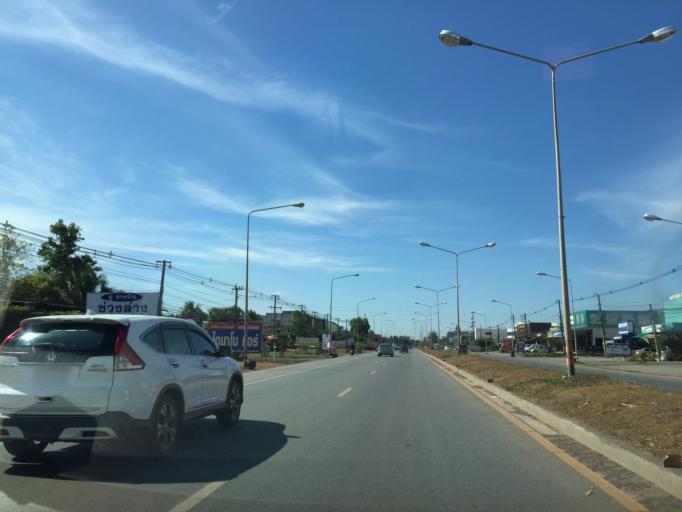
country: TH
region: Changwat Nong Bua Lamphu
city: Na Klang
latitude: 17.3030
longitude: 102.2001
